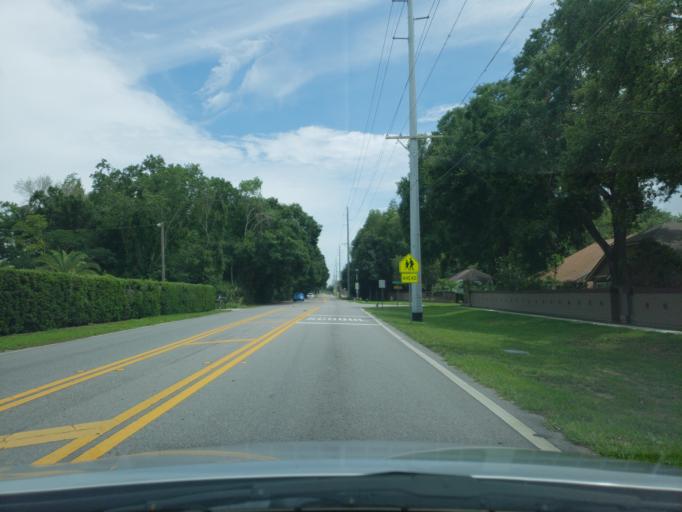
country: US
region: Florida
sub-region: Hillsborough County
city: Town 'n' Country
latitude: 28.0378
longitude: -82.5664
